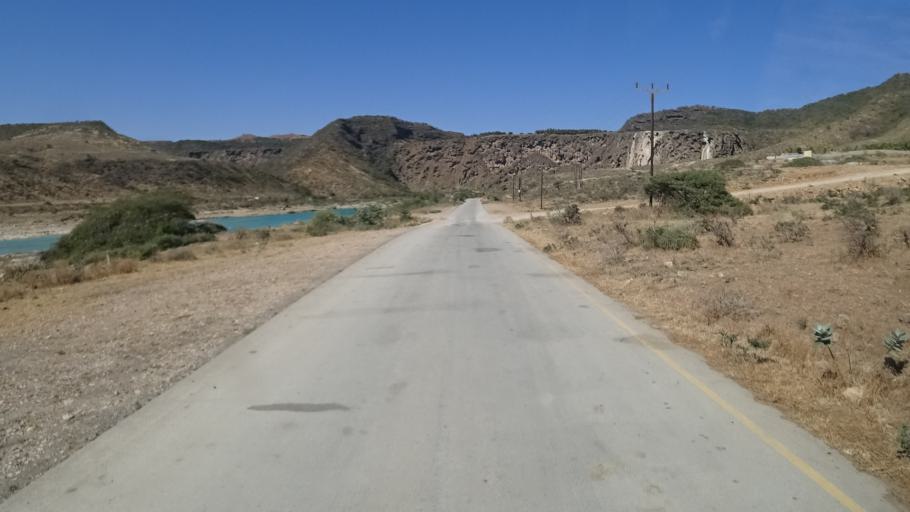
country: OM
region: Zufar
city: Salalah
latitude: 17.0682
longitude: 54.4316
